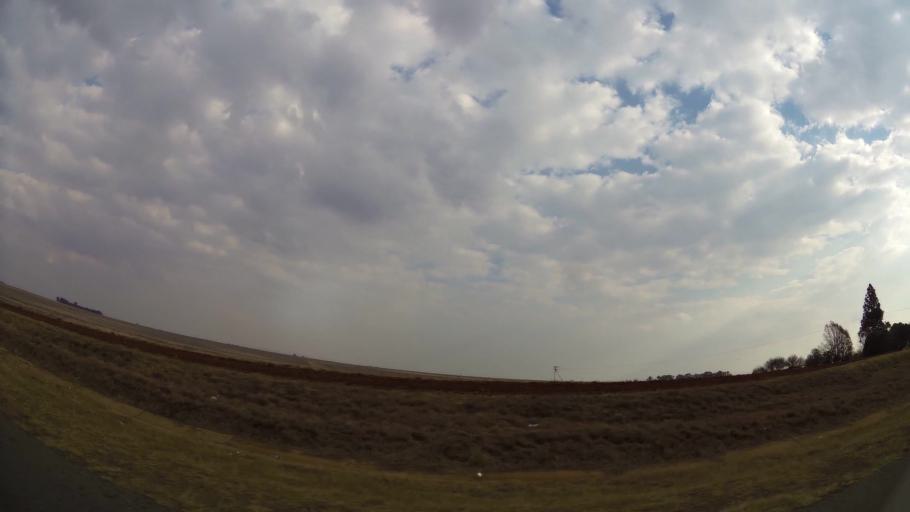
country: ZA
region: Gauteng
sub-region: Ekurhuleni Metropolitan Municipality
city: Nigel
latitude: -26.3113
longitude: 28.5765
